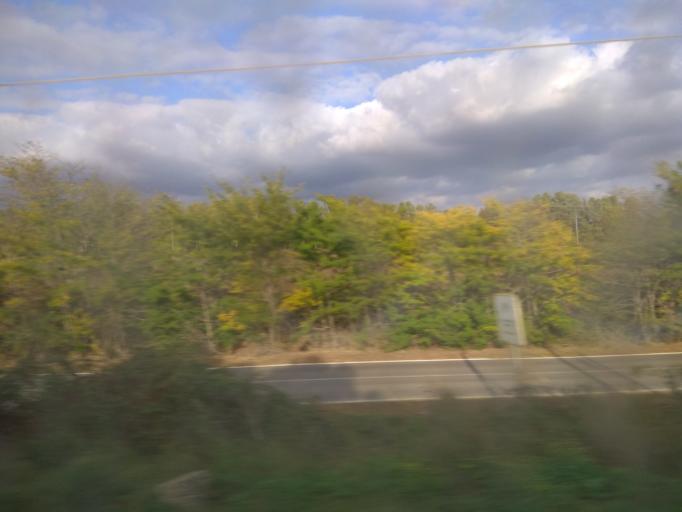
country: IT
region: Latium
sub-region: Citta metropolitana di Roma Capitale
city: Maccarese
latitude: 41.9106
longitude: 12.2056
